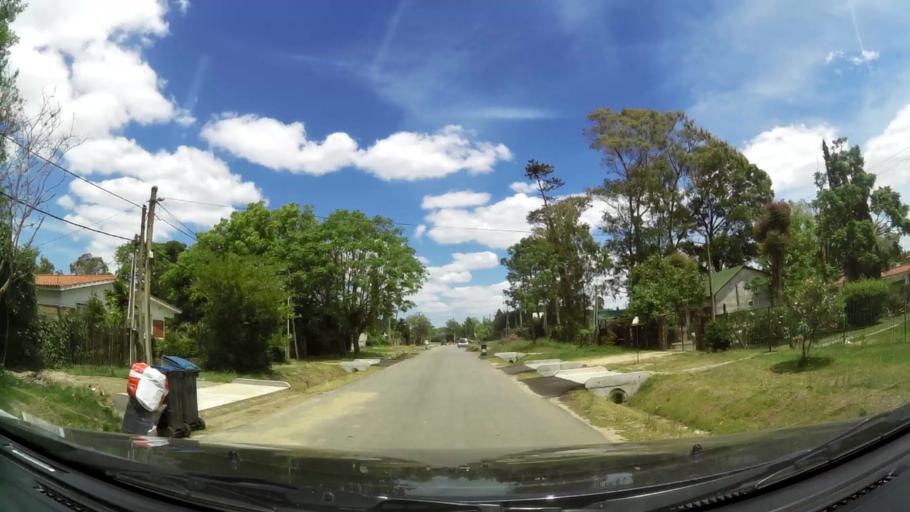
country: UY
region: Canelones
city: Colonia Nicolich
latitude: -34.8230
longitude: -55.9705
